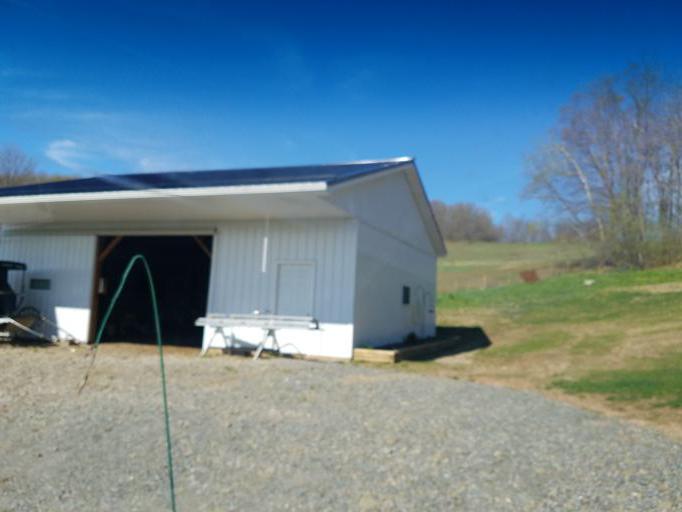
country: US
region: New York
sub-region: Allegany County
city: Andover
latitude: 41.9722
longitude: -77.7873
